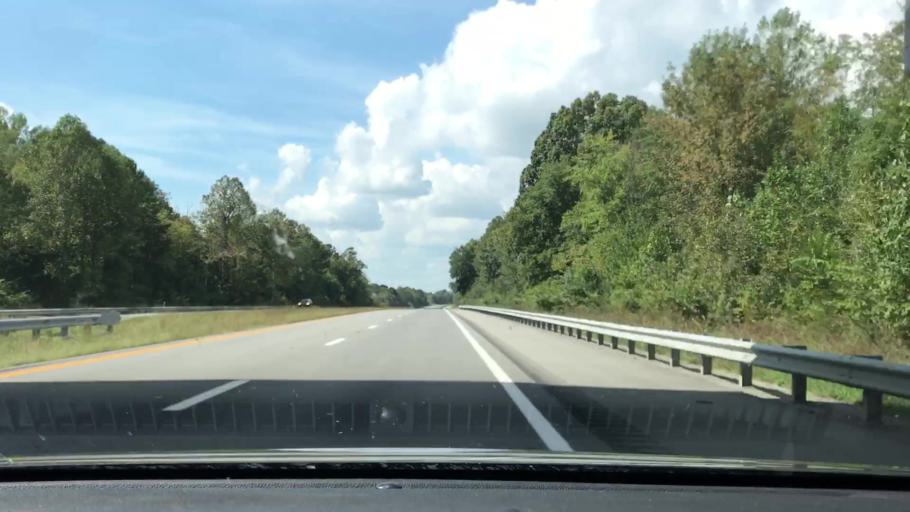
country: US
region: Kentucky
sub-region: Russell County
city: Russell Springs
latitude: 37.0460
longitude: -85.1286
